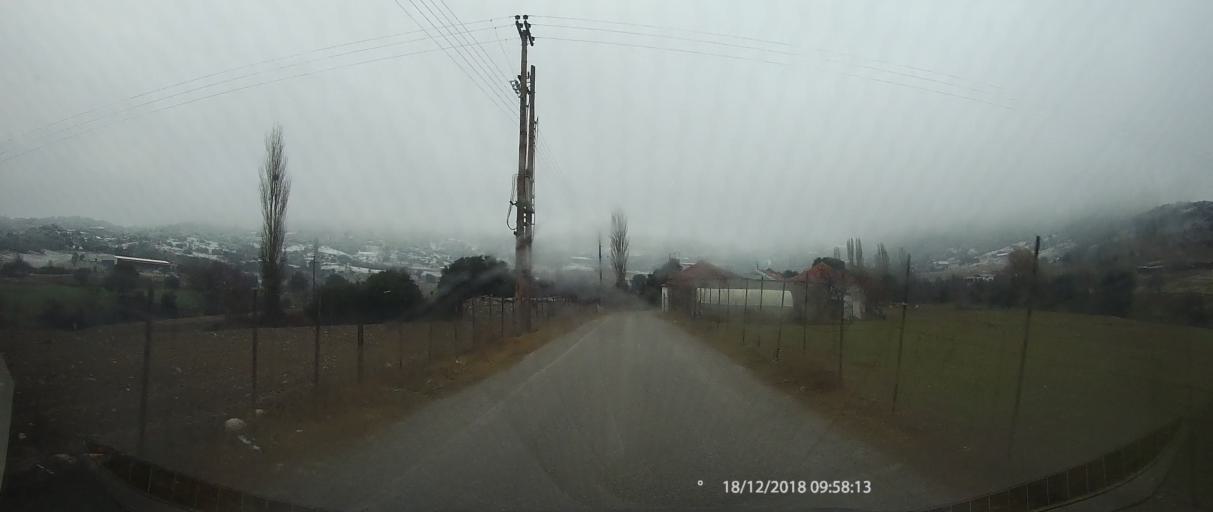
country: GR
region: Thessaly
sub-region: Nomos Larisis
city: Livadi
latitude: 40.0260
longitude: 22.2410
